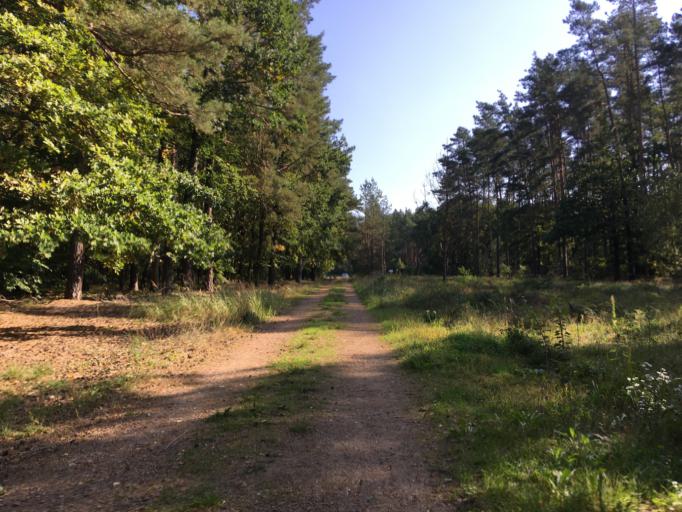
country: DE
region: Brandenburg
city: Wandlitz
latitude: 52.6929
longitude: 13.4401
